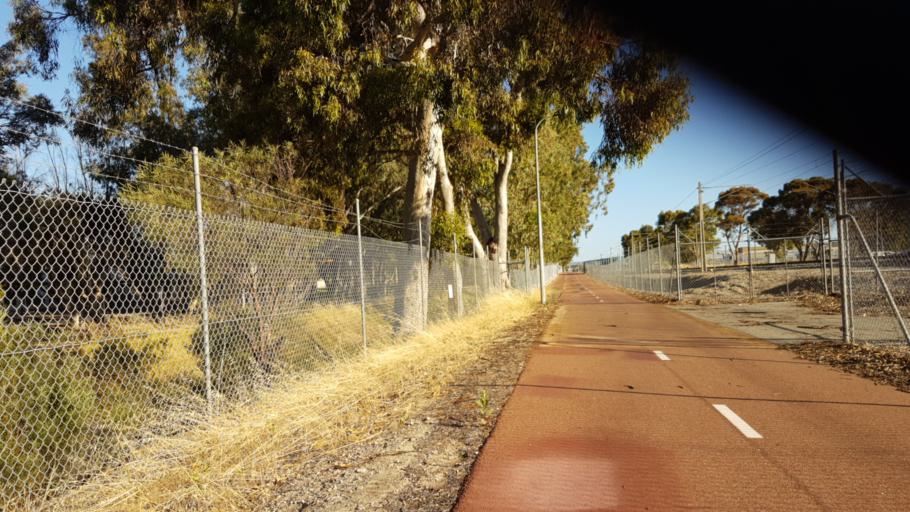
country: AU
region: Western Australia
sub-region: Gosnells
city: Kenwick
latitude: -32.0418
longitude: 115.9745
